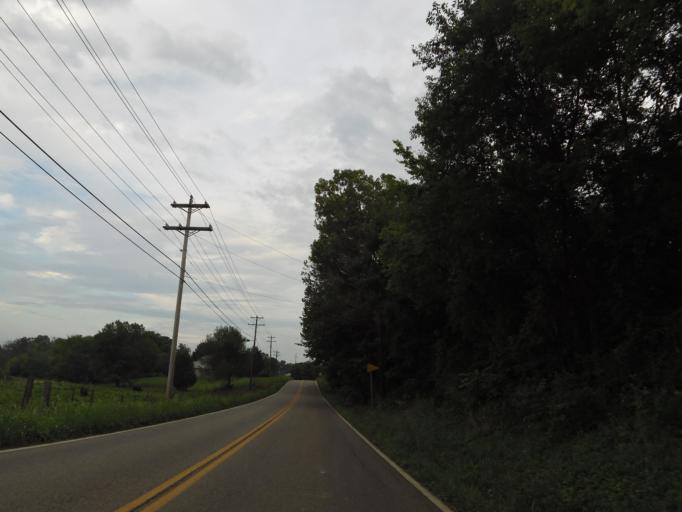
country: US
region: Tennessee
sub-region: Loudon County
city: Greenback
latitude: 35.6561
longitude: -84.1584
